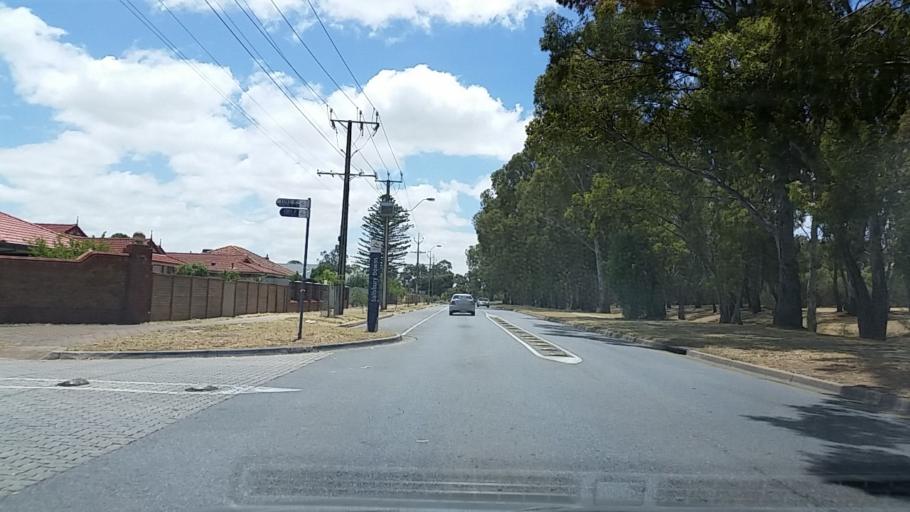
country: AU
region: South Australia
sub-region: Salisbury
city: Salisbury
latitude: -34.7709
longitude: 138.6179
